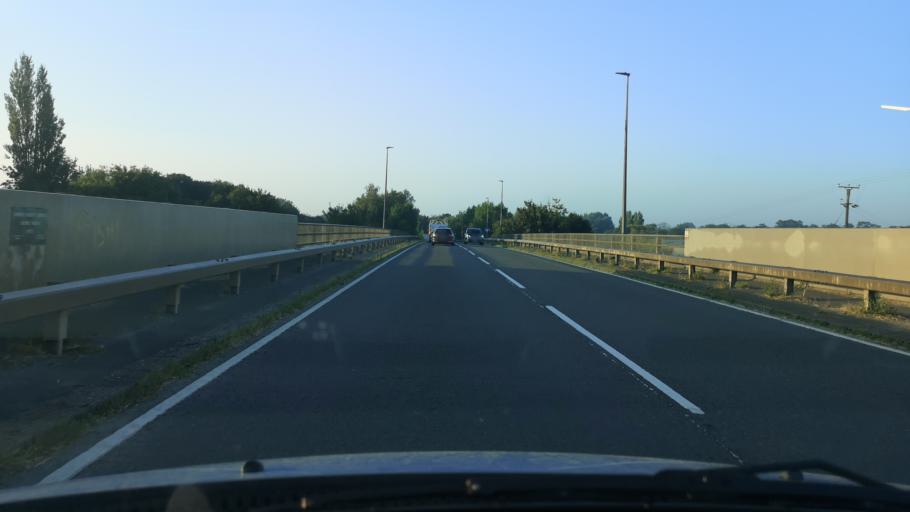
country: GB
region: England
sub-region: North Lincolnshire
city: Crowle
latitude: 53.5901
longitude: -0.8189
